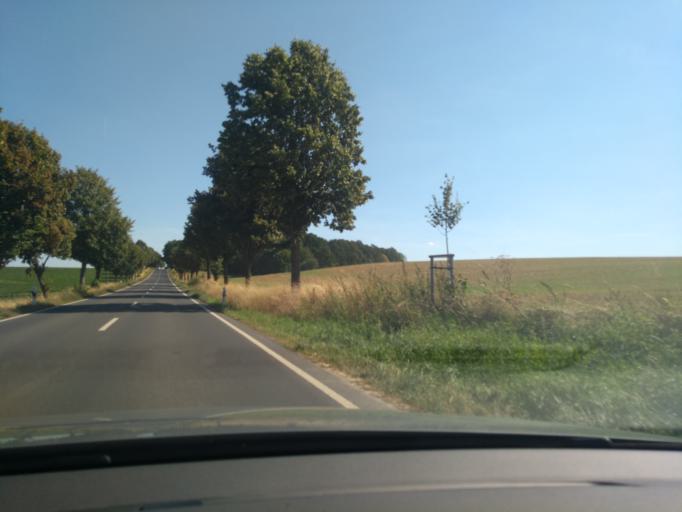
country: DE
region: Saxony
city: Crostwitz
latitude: 51.2189
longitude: 14.2566
